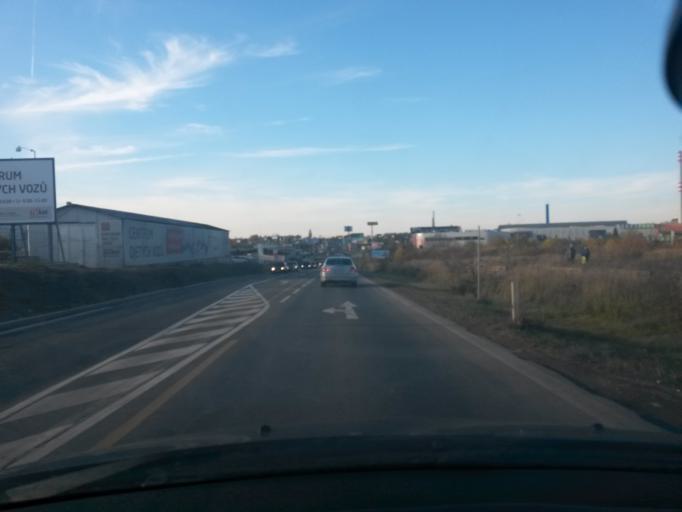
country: CZ
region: Praha
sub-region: Praha 14
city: Hostavice
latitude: 50.0672
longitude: 14.5471
